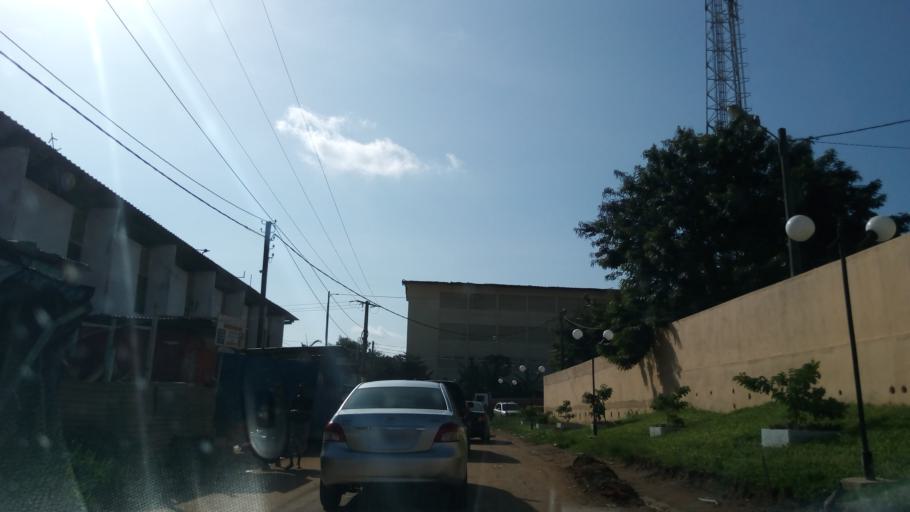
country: CI
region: Lagunes
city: Bingerville
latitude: 5.3586
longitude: -3.8900
